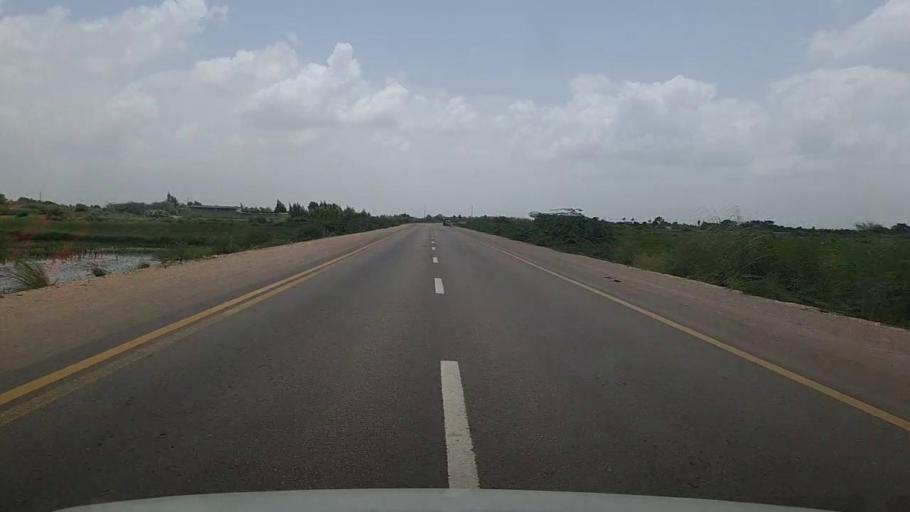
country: PK
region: Sindh
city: Thatta
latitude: 24.7543
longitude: 67.9527
